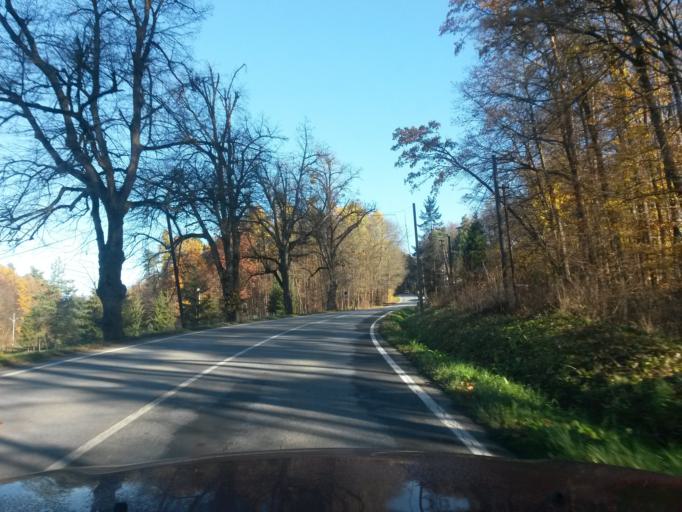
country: SK
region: Presovsky
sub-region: Okres Presov
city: Presov
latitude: 48.9867
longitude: 21.1757
